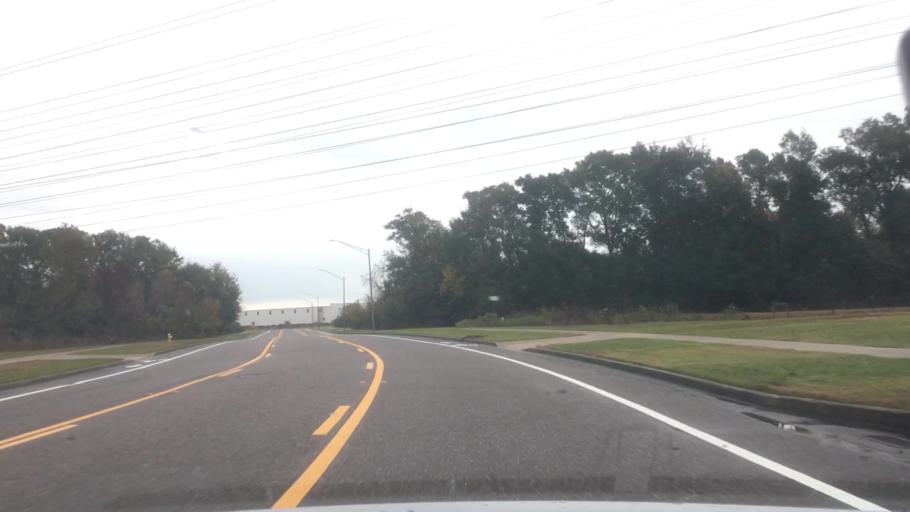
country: US
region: Florida
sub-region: Duval County
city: Jacksonville
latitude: 30.4488
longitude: -81.5753
